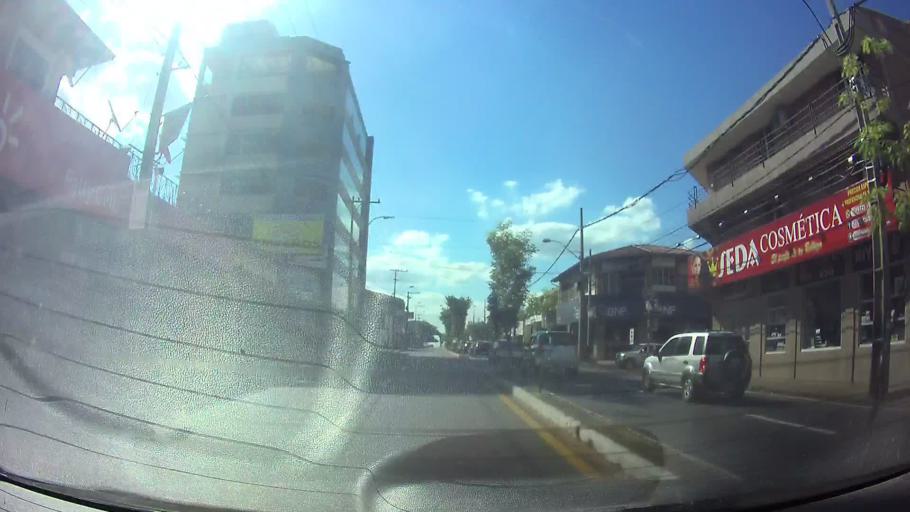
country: PY
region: Central
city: Itaugua
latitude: -25.3943
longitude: -57.3509
